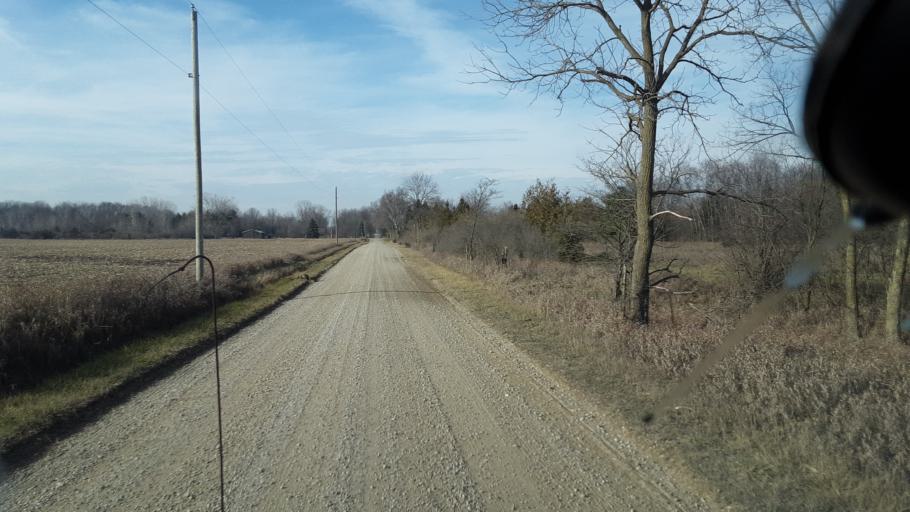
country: US
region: Ohio
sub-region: Defiance County
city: Hicksville
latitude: 41.2706
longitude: -84.8235
